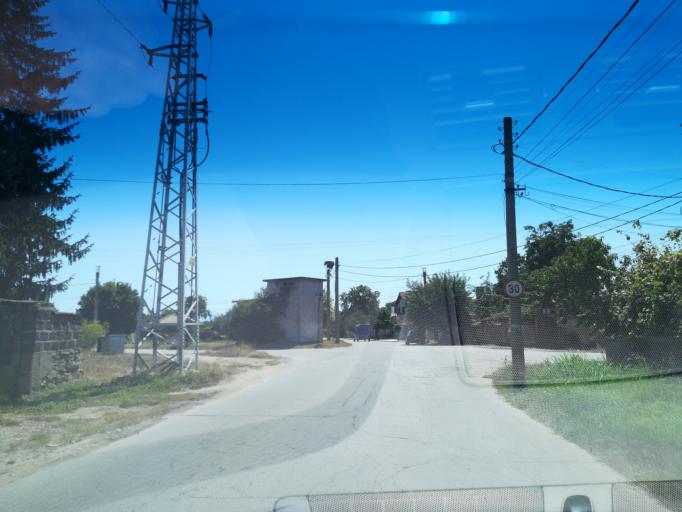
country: BG
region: Pazardzhik
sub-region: Obshtina Pazardzhik
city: Pazardzhik
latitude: 42.2799
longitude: 24.3949
